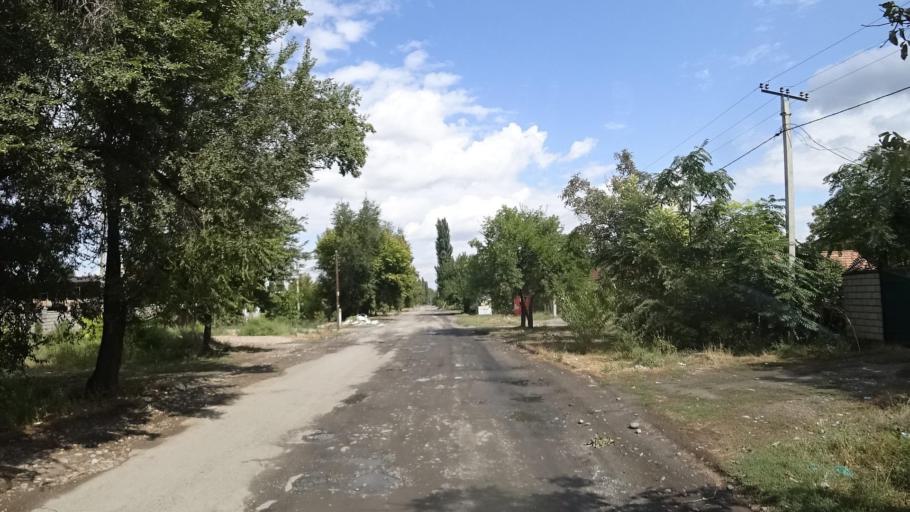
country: KG
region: Chuy
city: Lebedinovka
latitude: 42.8779
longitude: 74.7203
